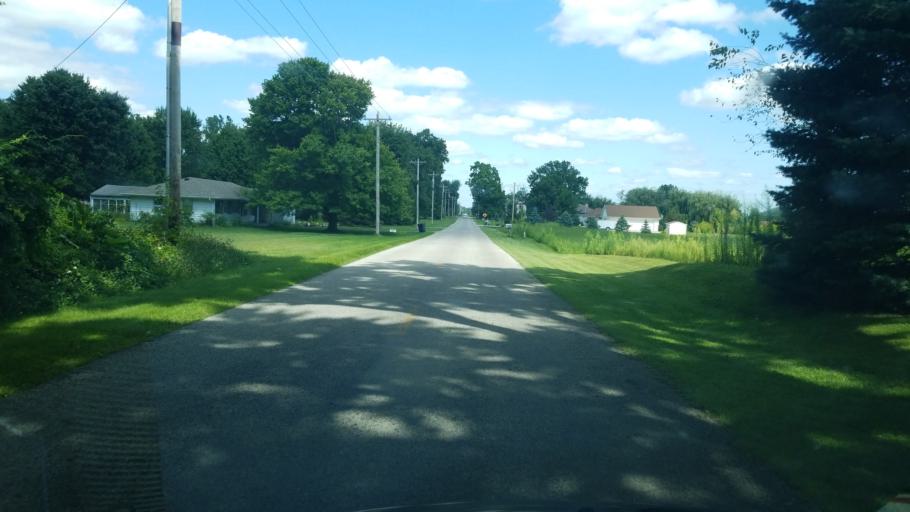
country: US
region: Ohio
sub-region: Henry County
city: Liberty Center
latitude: 41.4974
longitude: -83.9413
